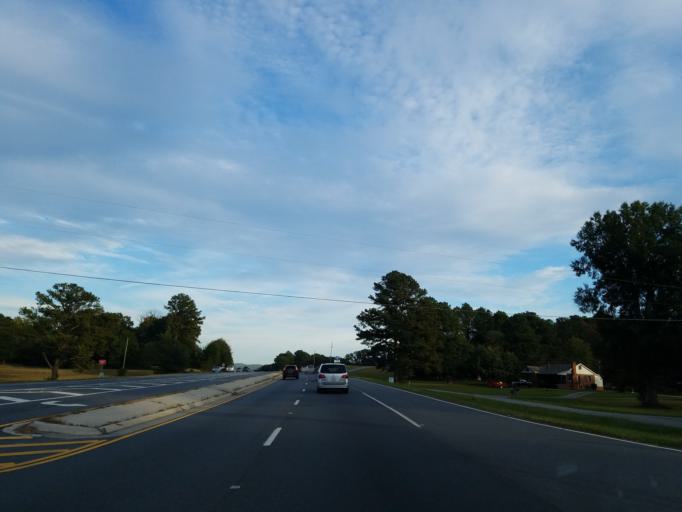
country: US
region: Georgia
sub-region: Bartow County
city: Cartersville
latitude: 34.2101
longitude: -84.8287
